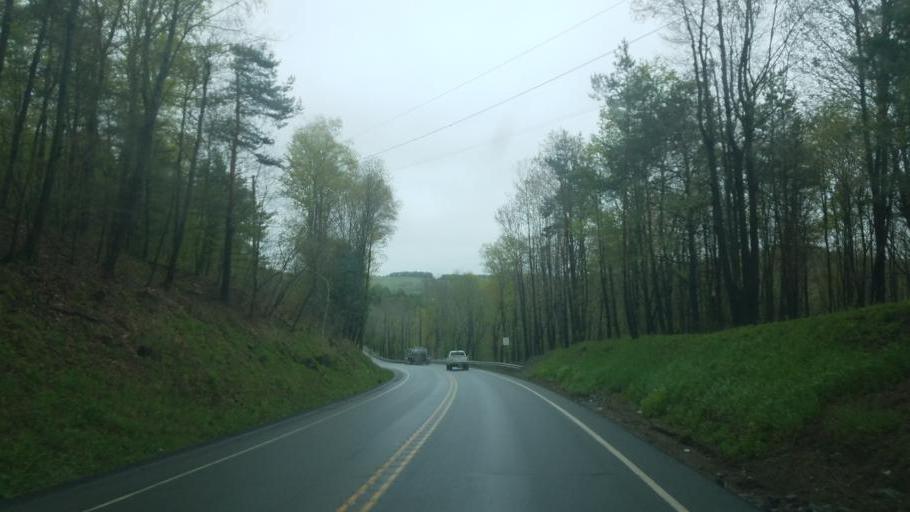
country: US
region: Pennsylvania
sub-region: McKean County
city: Port Allegany
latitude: 41.8278
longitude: -78.3086
